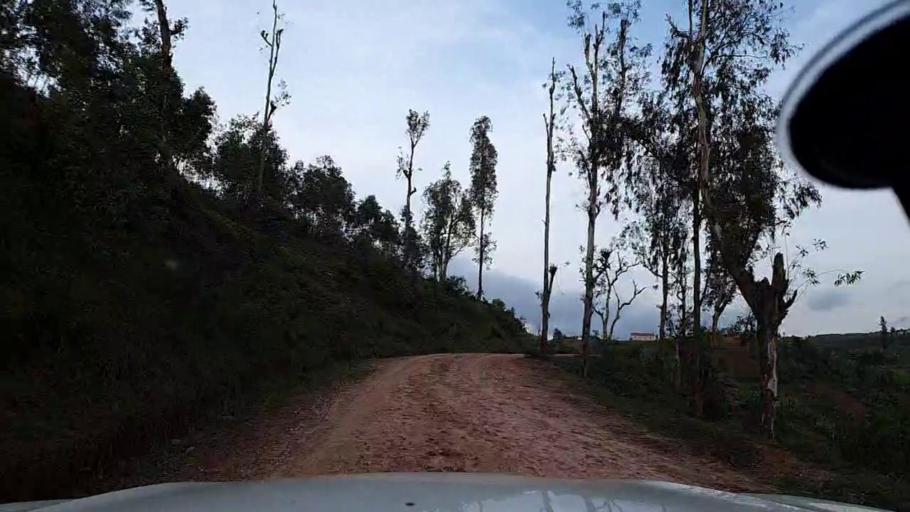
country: RW
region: Southern Province
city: Nyanza
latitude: -2.2101
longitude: 29.6016
